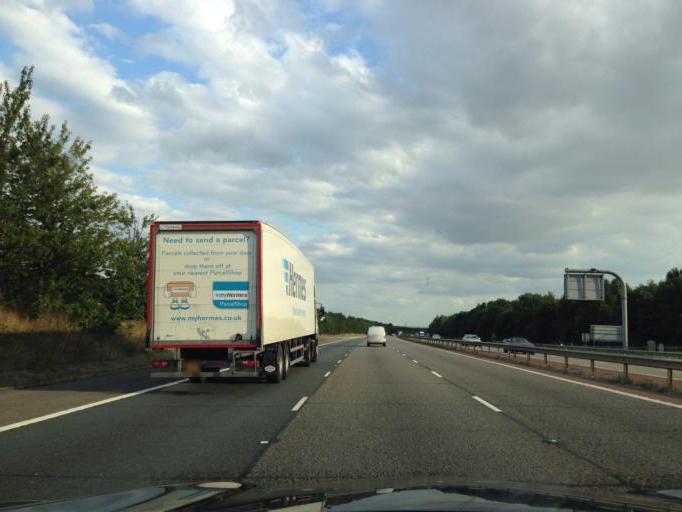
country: GB
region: England
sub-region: Oxfordshire
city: Banbury
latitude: 52.0704
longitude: -1.3116
